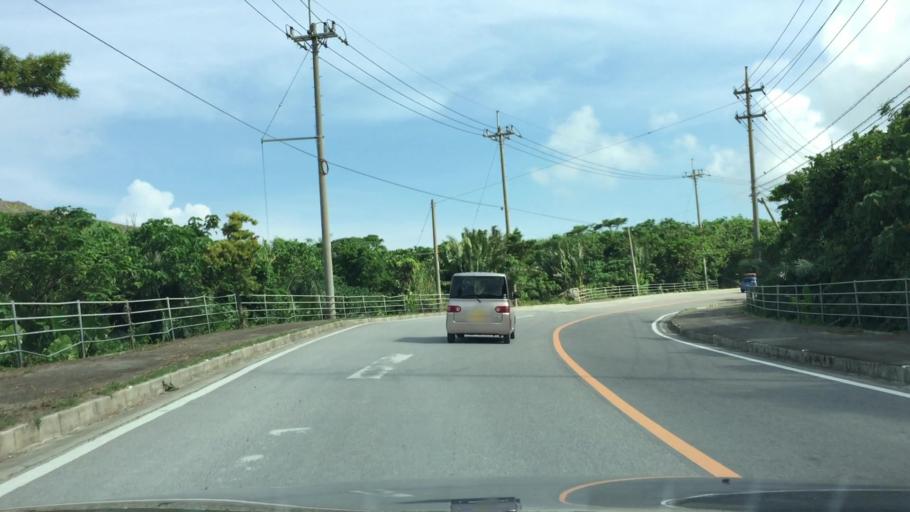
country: JP
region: Okinawa
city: Ishigaki
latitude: 24.4306
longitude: 124.2477
